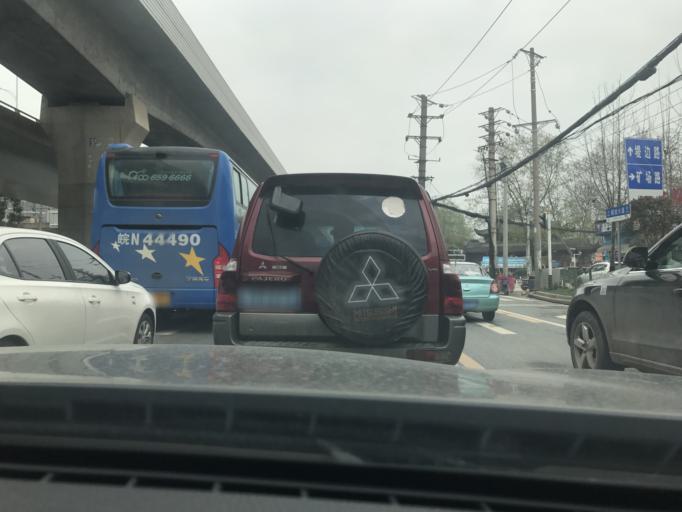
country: CN
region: Hubei
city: Houhu
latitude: 30.6603
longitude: 114.3299
